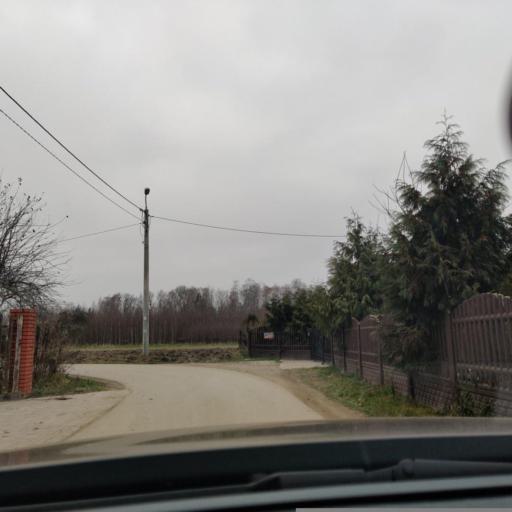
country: PL
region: Lodz Voivodeship
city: Zabia Wola
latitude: 52.0251
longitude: 20.6355
